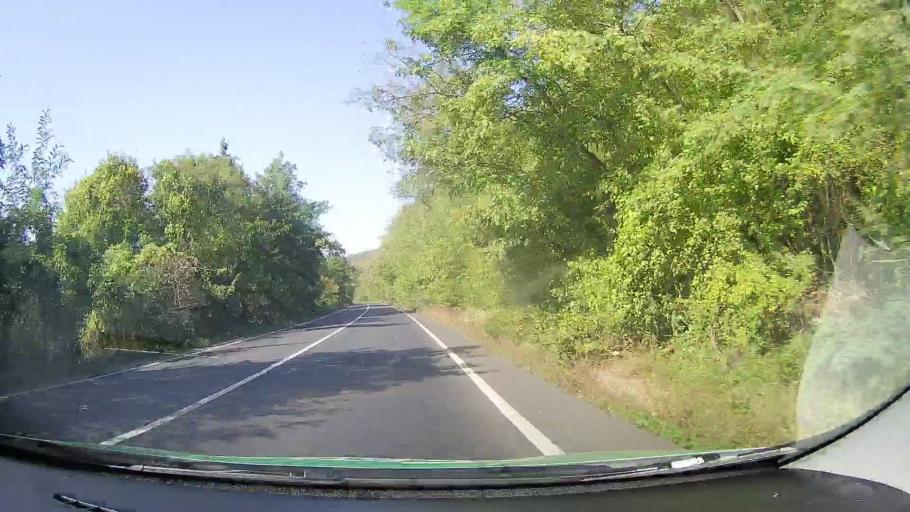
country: RO
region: Arad
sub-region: Comuna Savarsin
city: Savarsin
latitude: 46.0126
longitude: 22.2663
